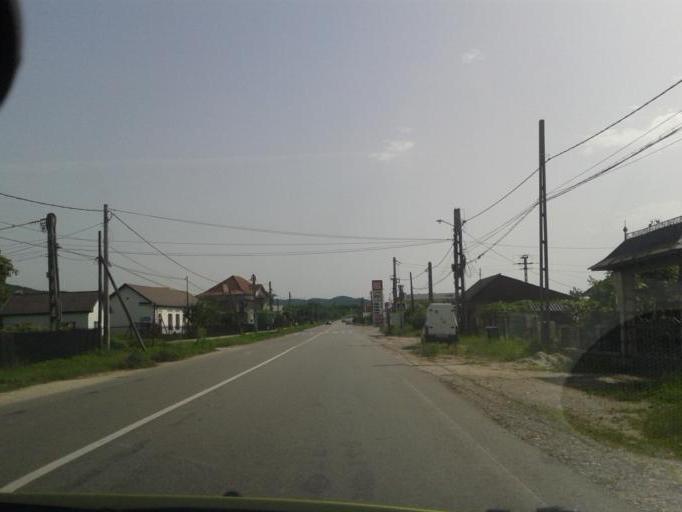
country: RO
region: Valcea
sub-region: Municipiul Ramnicu Valcea
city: Stolniceni
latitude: 45.0549
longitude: 24.2862
